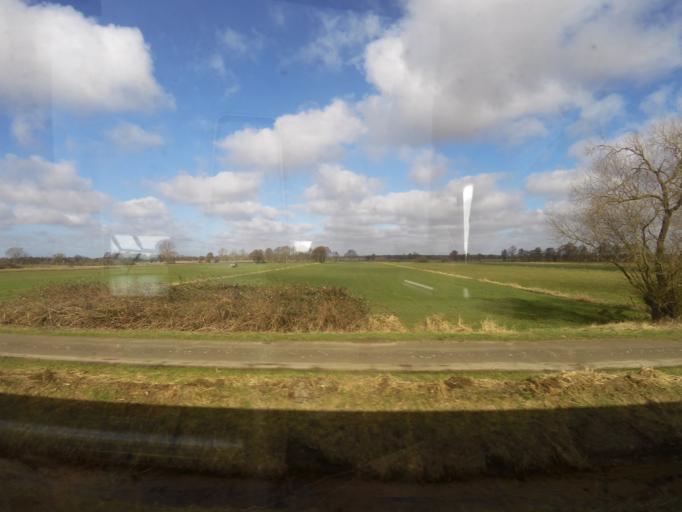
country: DE
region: Lower Saxony
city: Ottersberg
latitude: 53.0926
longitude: 9.0824
